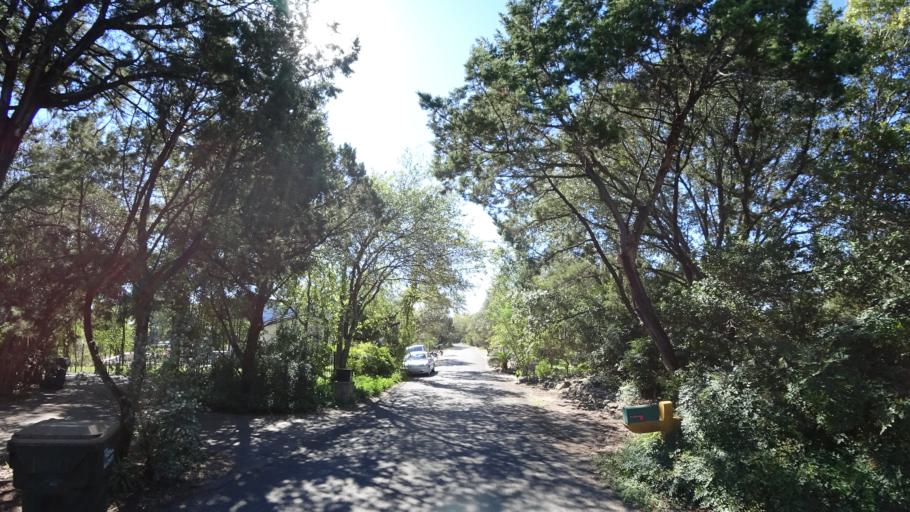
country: US
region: Texas
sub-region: Travis County
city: West Lake Hills
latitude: 30.3165
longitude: -97.8049
